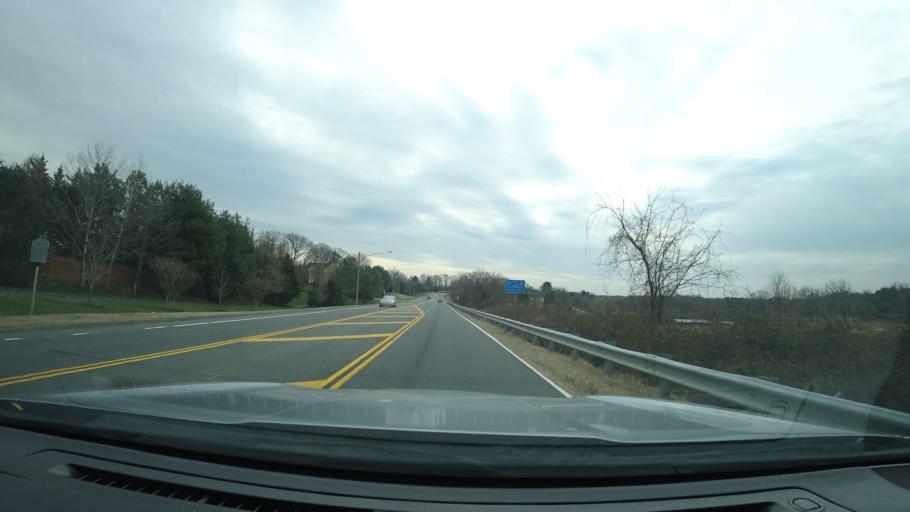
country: US
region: Virginia
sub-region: Fairfax County
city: Reston
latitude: 38.9743
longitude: -77.3155
